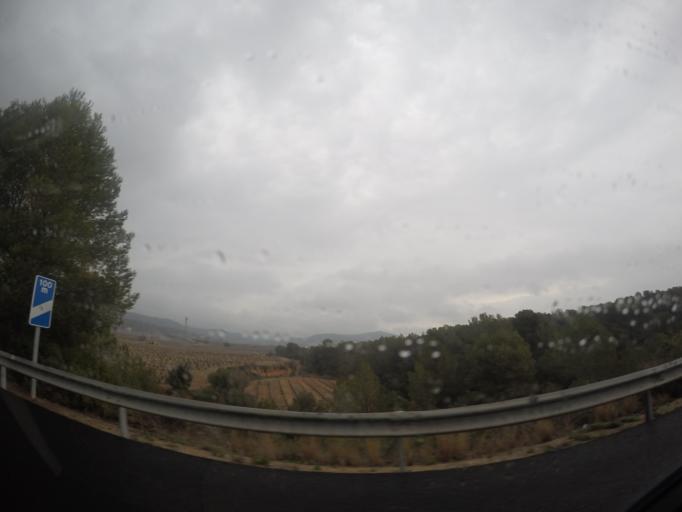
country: ES
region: Catalonia
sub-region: Provincia de Tarragona
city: la Bisbal del Penedes
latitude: 41.2780
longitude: 1.5094
